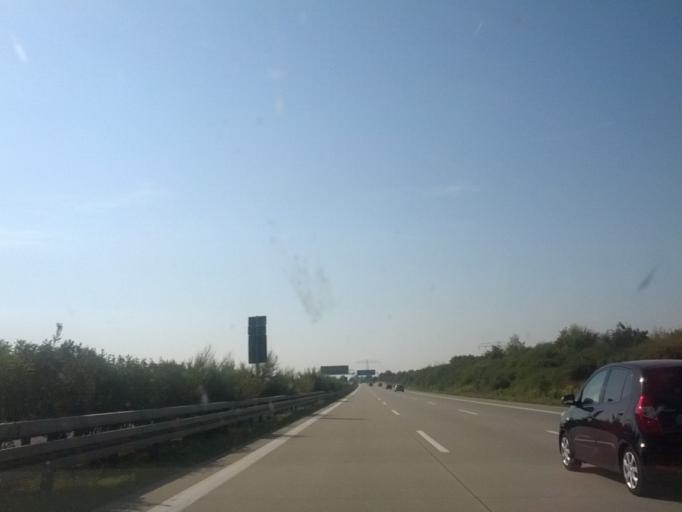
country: DE
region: Brandenburg
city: Woltersdorf
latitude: 52.4869
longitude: 13.7540
